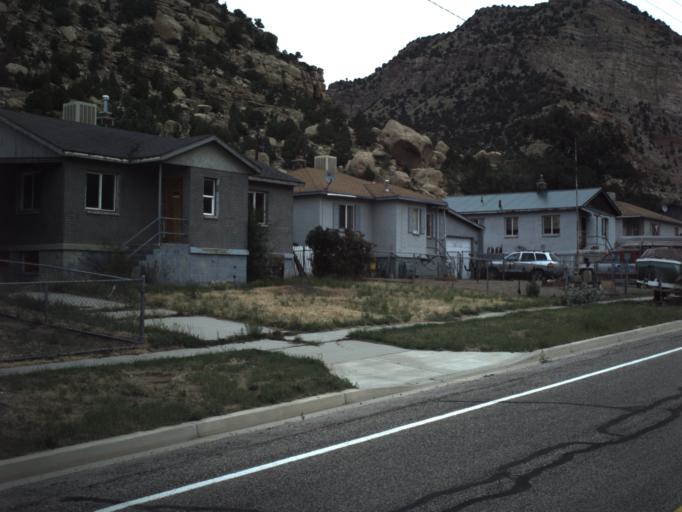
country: US
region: Utah
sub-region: Carbon County
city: East Carbon City
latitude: 39.5549
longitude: -110.3815
